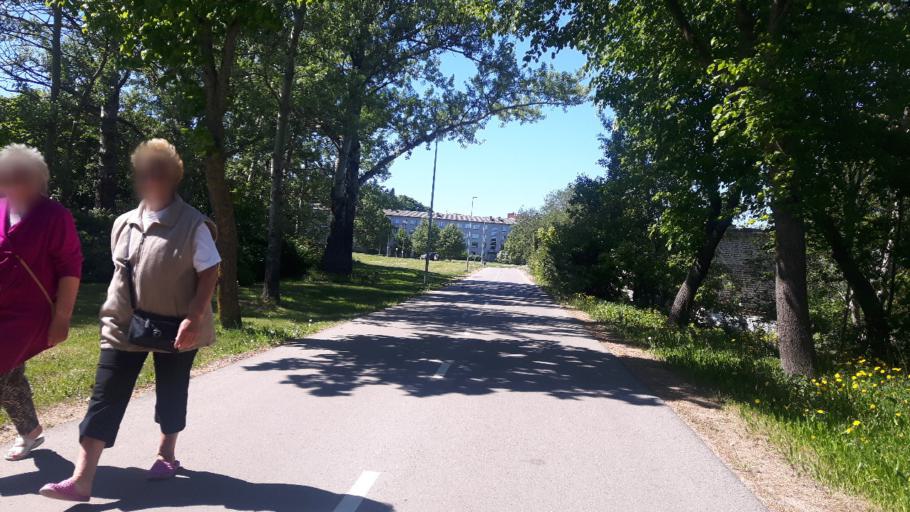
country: EE
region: Ida-Virumaa
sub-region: Sillamaee linn
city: Sillamae
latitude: 59.3967
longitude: 27.7814
